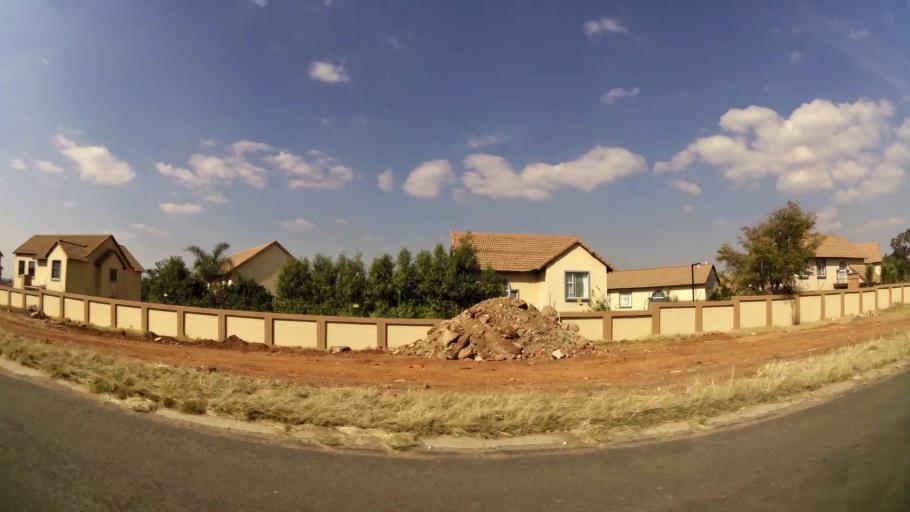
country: ZA
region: Gauteng
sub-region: Ekurhuleni Metropolitan Municipality
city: Tembisa
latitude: -26.0830
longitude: 28.2609
